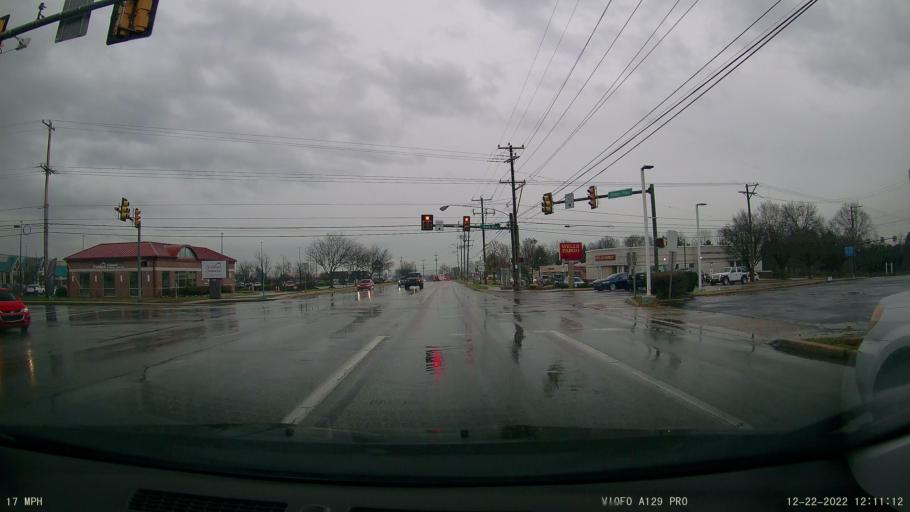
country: US
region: Pennsylvania
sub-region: Montgomery County
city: Trooper
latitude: 40.1472
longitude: -75.3956
